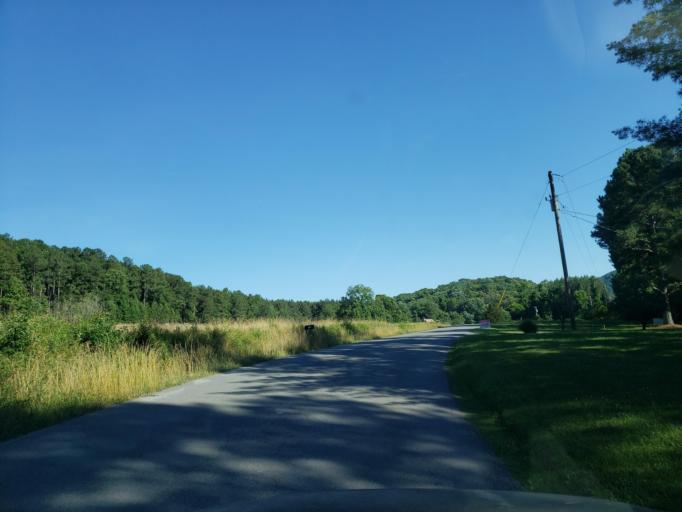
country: US
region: Georgia
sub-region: Whitfield County
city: Dalton
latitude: 34.6599
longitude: -85.0924
